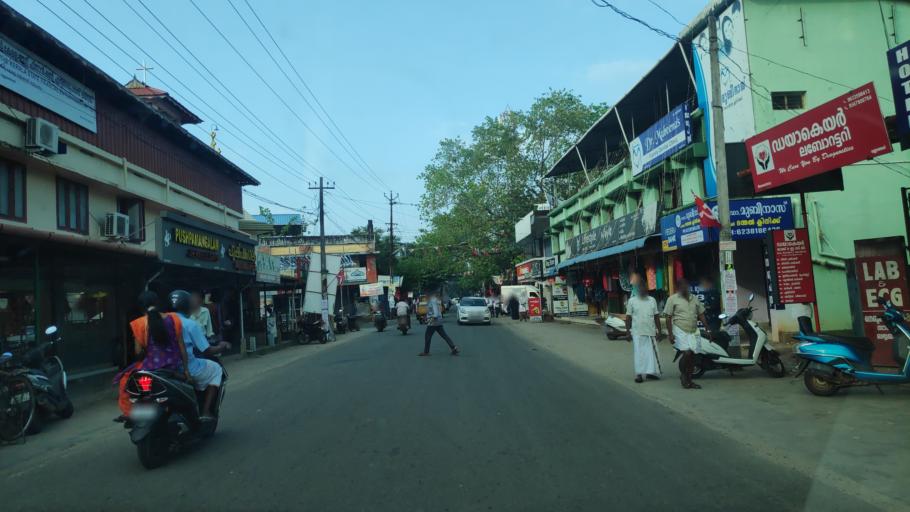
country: IN
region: Kerala
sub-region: Alappuzha
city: Alleppey
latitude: 9.5716
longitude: 76.3476
